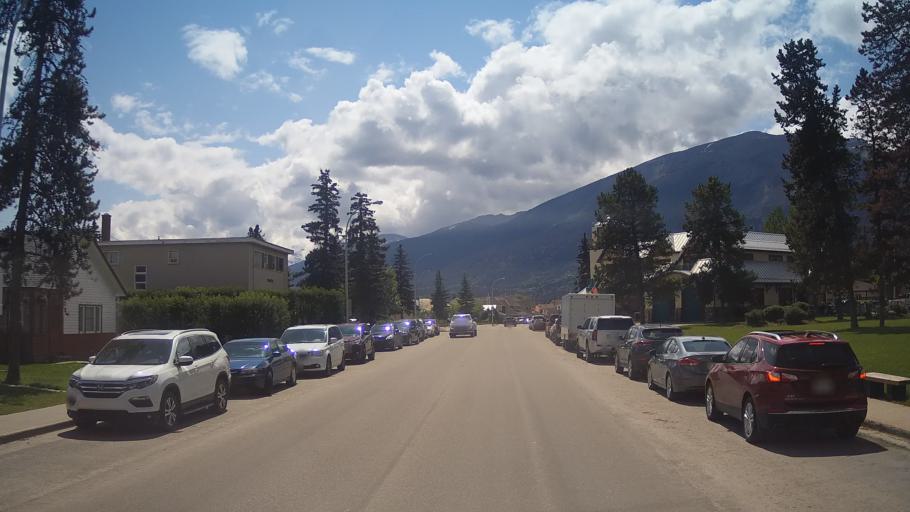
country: CA
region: Alberta
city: Jasper Park Lodge
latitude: 52.8770
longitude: -118.0826
